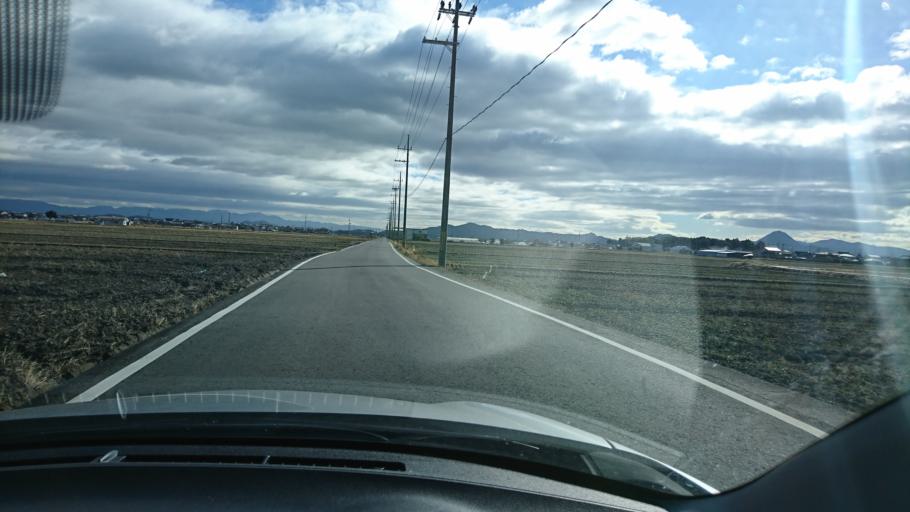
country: JP
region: Shiga Prefecture
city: Moriyama
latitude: 35.1233
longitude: 136.0049
